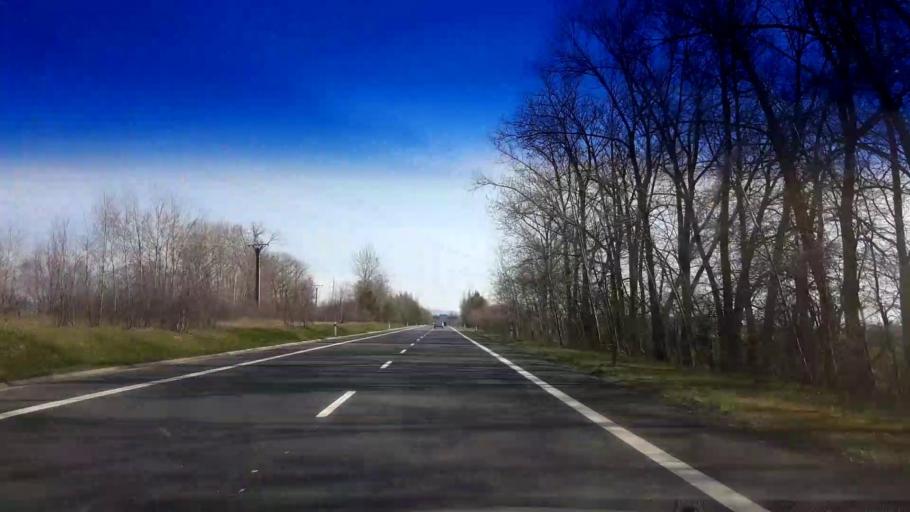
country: CZ
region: Karlovarsky
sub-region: Okres Cheb
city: Frantiskovy Lazne
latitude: 50.0974
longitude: 12.3305
